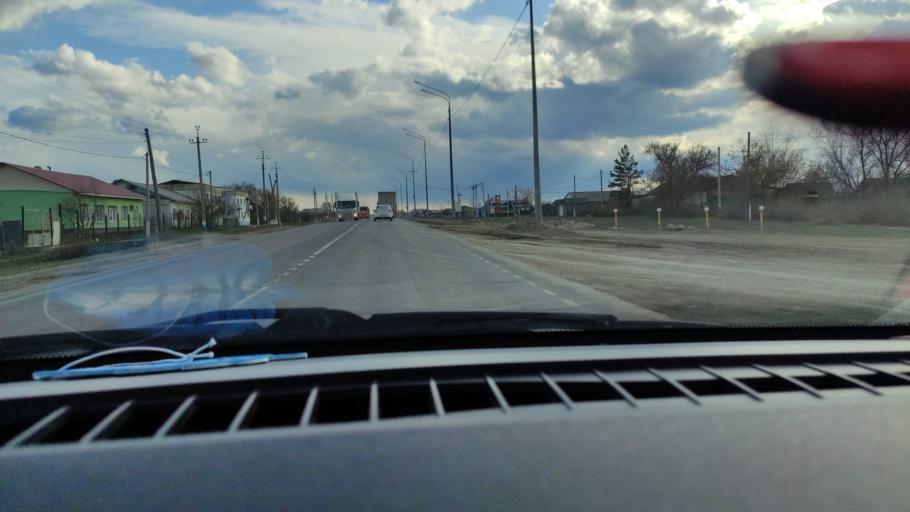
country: RU
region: Saratov
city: Sinodskoye
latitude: 51.9882
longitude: 46.6658
